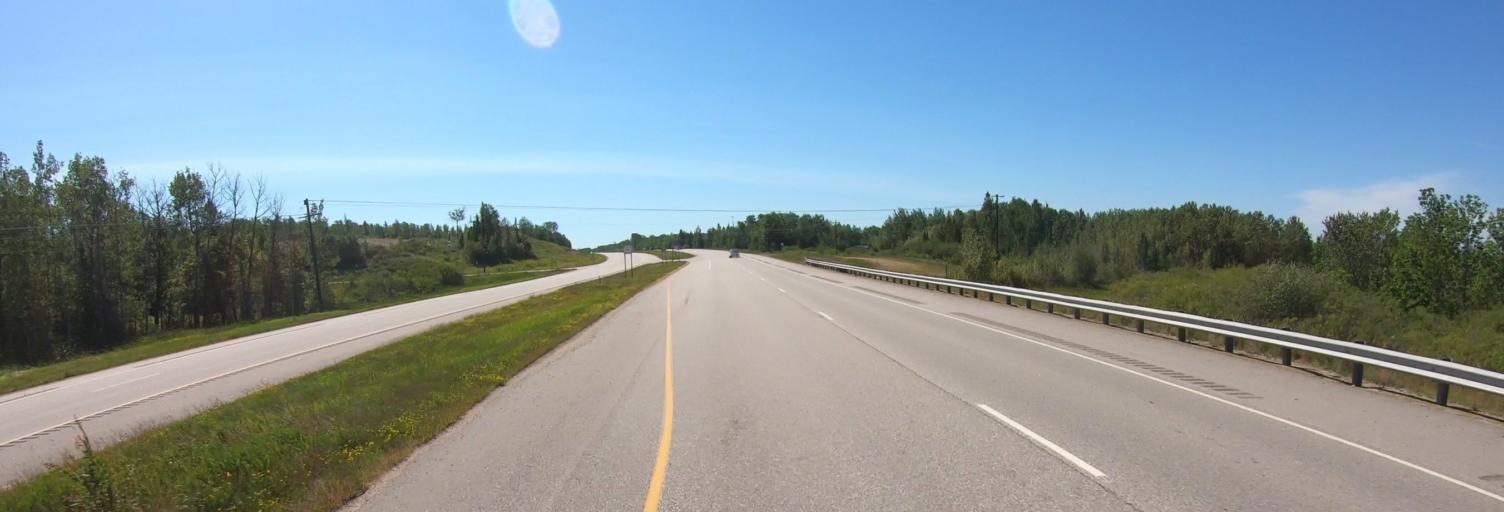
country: US
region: Minnesota
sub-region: Saint Louis County
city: Mountain Iron
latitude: 47.7711
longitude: -92.6552
